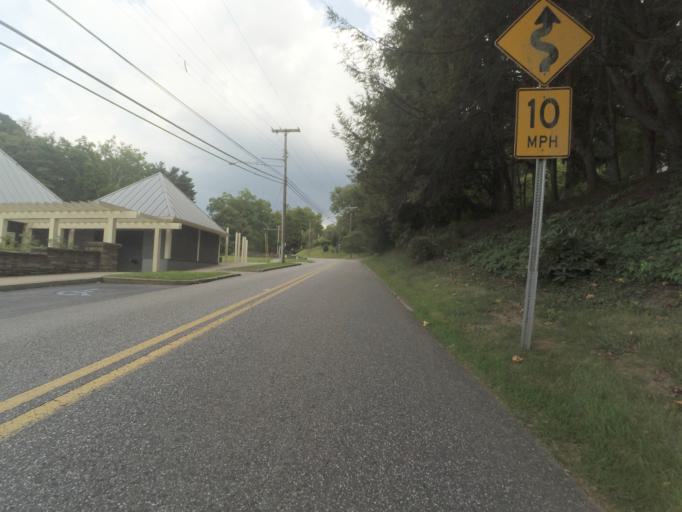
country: US
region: West Virginia
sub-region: Cabell County
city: Huntington
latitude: 38.4061
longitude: -82.4406
